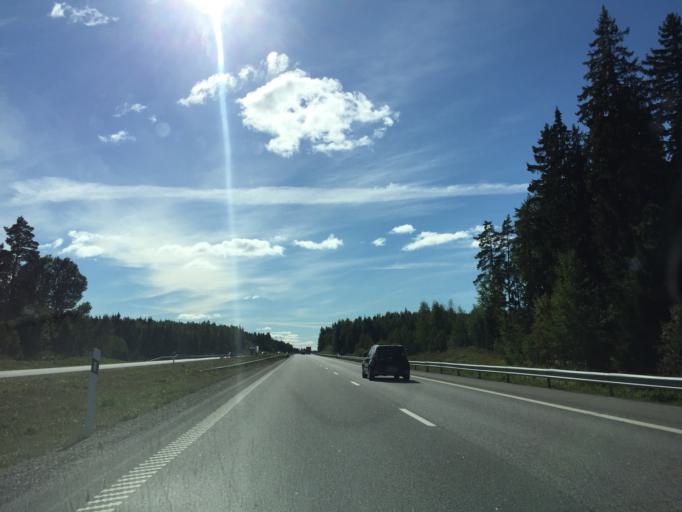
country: SE
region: OErebro
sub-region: Lindesbergs Kommun
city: Fellingsbro
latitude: 59.3630
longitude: 15.5727
